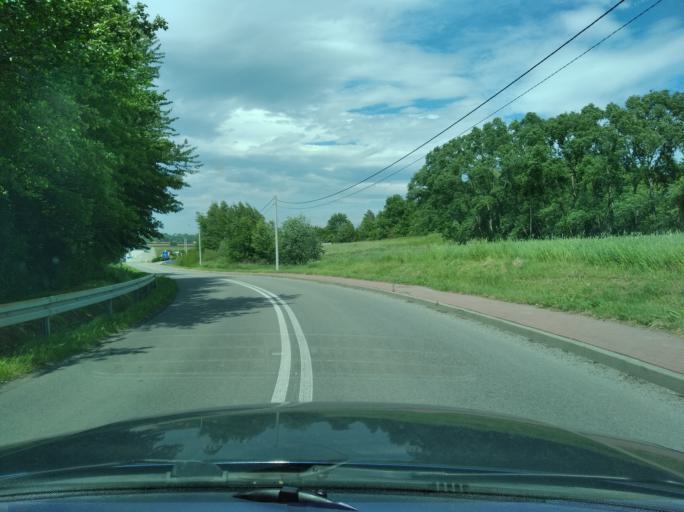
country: PL
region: Subcarpathian Voivodeship
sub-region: Powiat ropczycko-sedziszowski
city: Ropczyce
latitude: 50.0476
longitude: 21.6222
